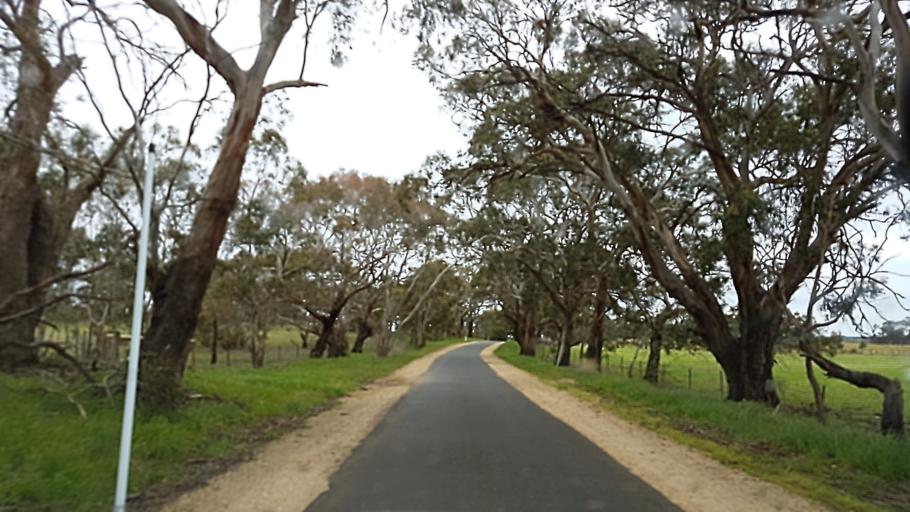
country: AU
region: Victoria
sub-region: Ballarat North
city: Mount Clear
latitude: -37.7732
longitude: 144.0745
